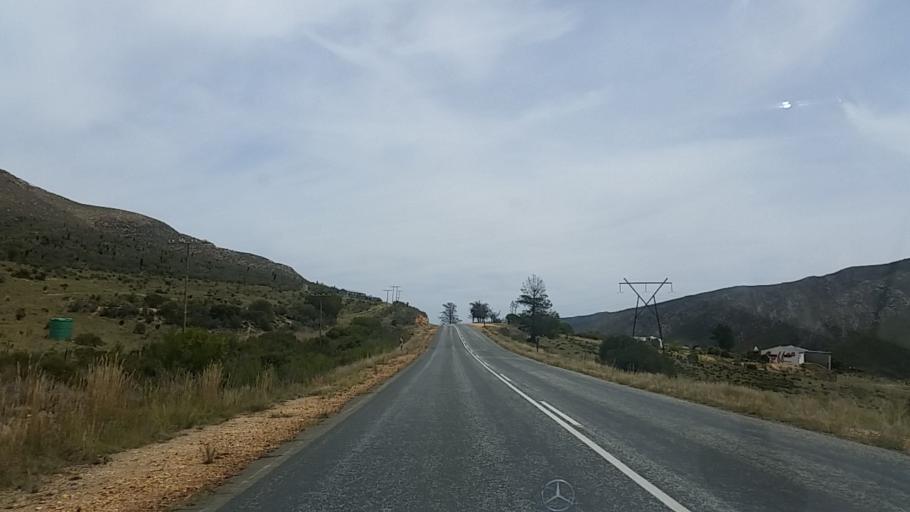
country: ZA
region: Western Cape
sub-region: Eden District Municipality
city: Knysna
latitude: -33.7440
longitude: 22.9945
